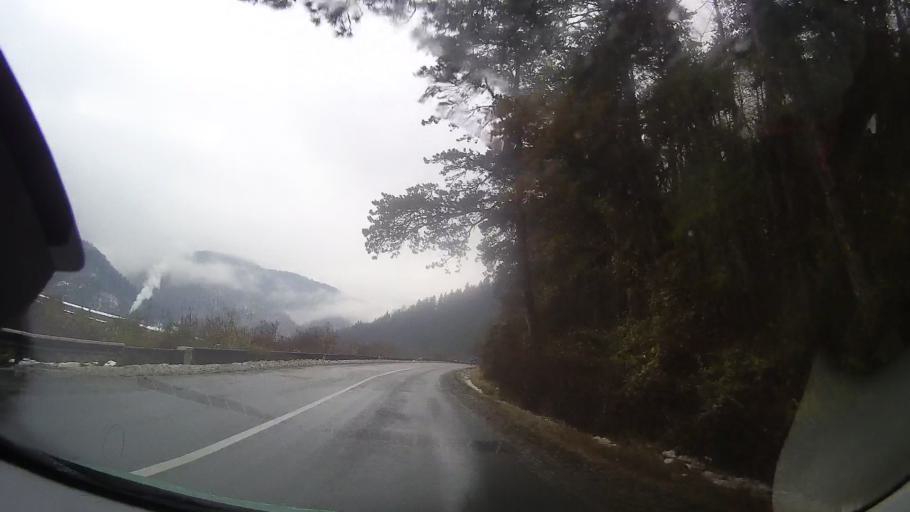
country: RO
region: Neamt
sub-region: Comuna Tarcau
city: Tarcau
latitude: 46.8929
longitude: 26.1372
